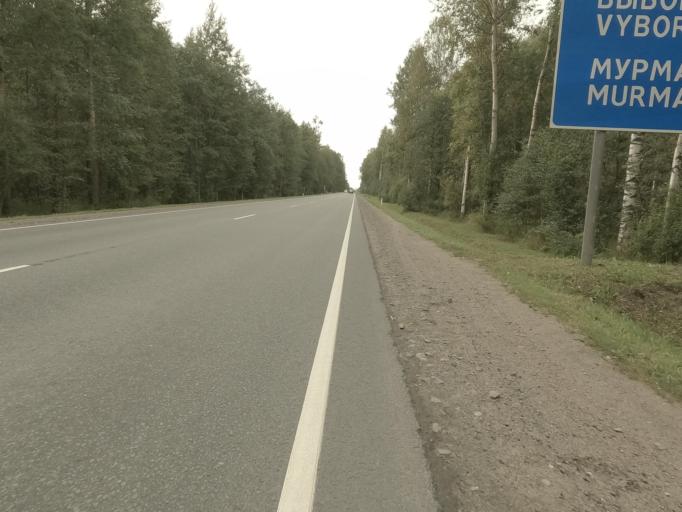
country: RU
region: Leningrad
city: Kirovsk
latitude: 59.8481
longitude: 31.0345
